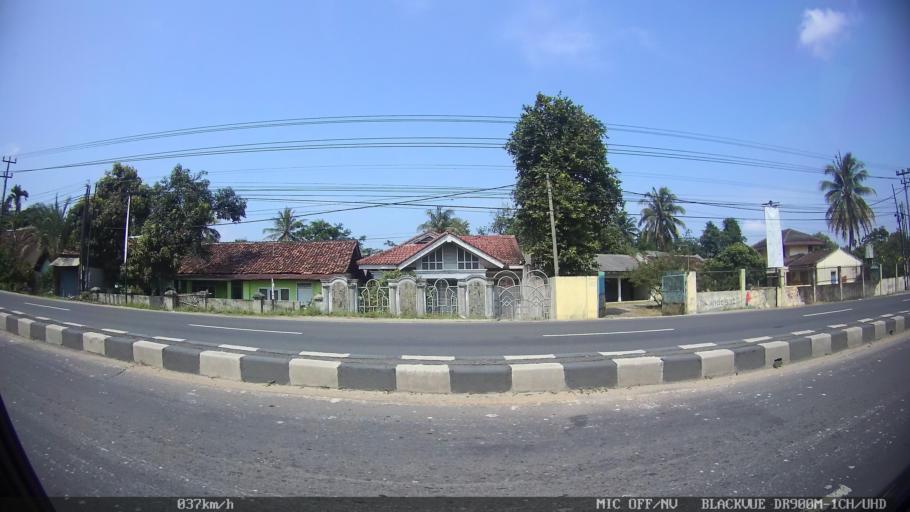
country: ID
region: Lampung
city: Natar
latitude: -5.2810
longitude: 105.1889
